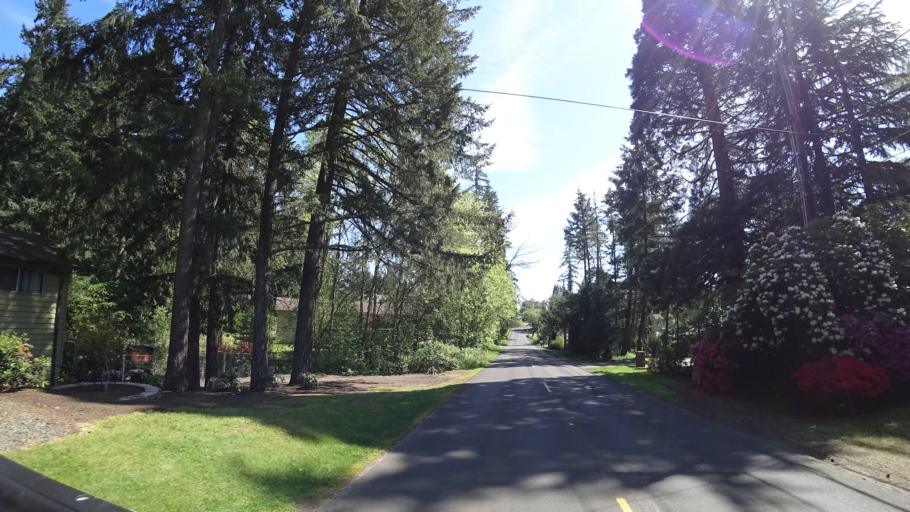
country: US
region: Oregon
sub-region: Washington County
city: Hillsboro
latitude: 45.5168
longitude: -122.9581
